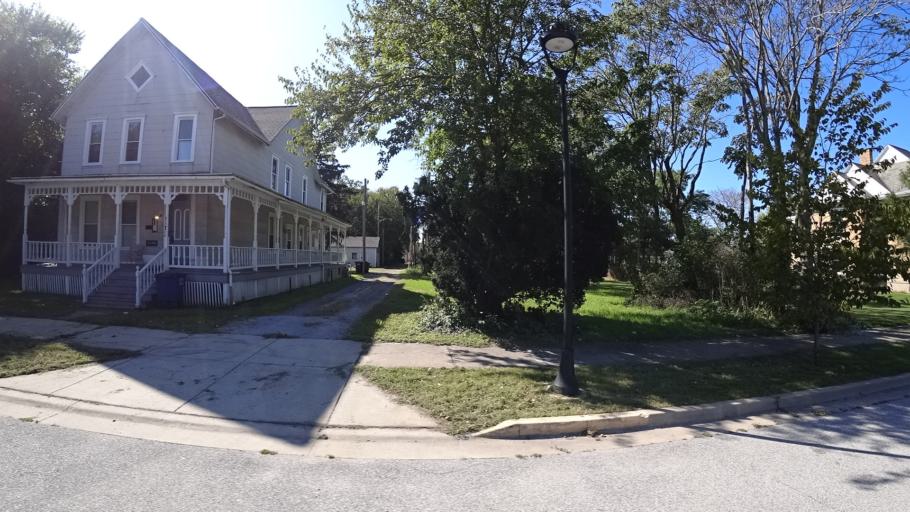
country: US
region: Indiana
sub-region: LaPorte County
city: Michigan City
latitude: 41.7154
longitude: -86.8976
